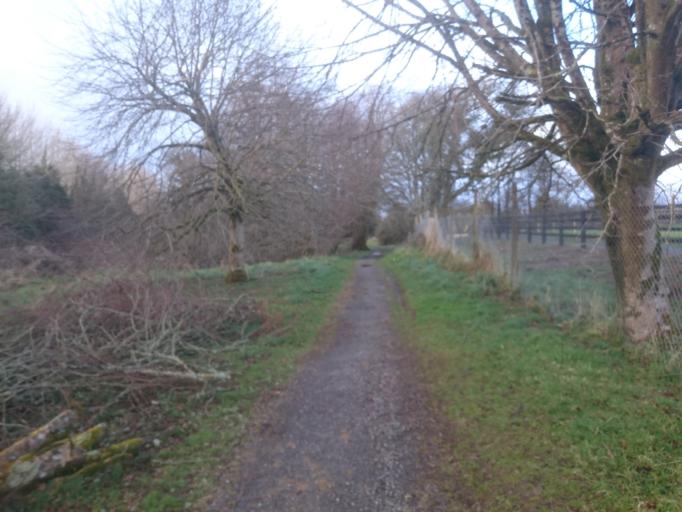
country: IE
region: Connaught
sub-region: Roscommon
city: Castlerea
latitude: 53.7698
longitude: -8.4854
